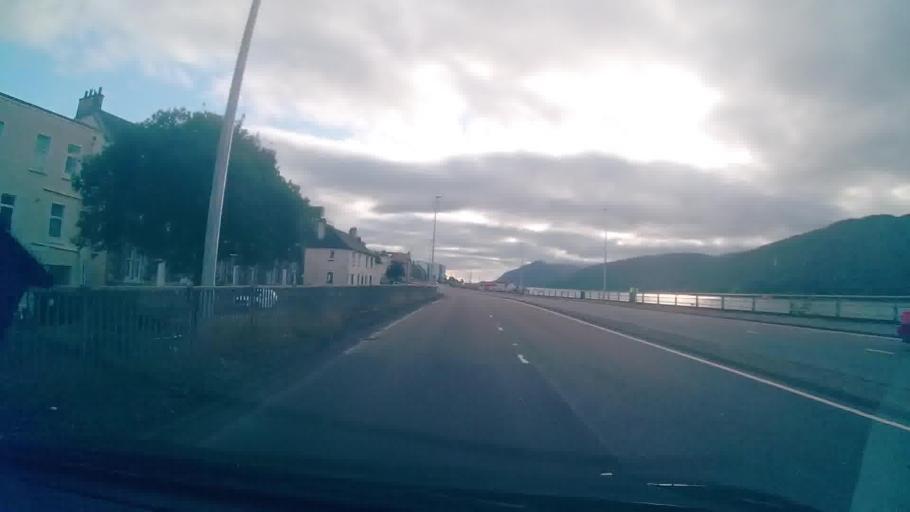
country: GB
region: Scotland
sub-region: Highland
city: Fort William
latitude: 56.8198
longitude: -5.1130
